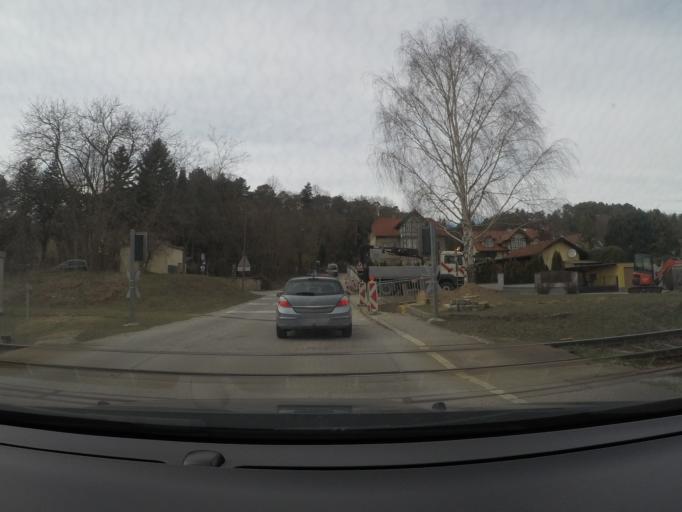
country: AT
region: Lower Austria
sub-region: Politischer Bezirk Neunkirchen
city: Pitten
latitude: 47.7211
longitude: 16.1831
